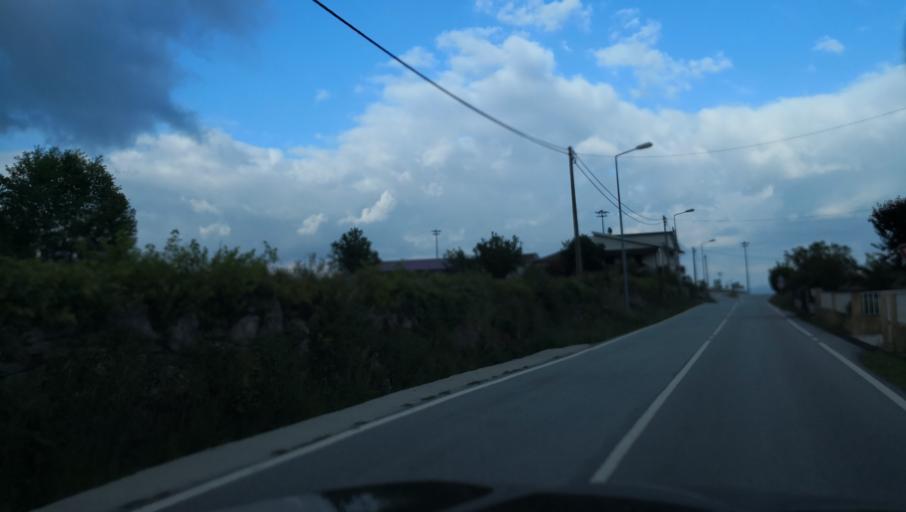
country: PT
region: Vila Real
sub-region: Vila Real
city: Vila Real
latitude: 41.2846
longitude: -7.8089
